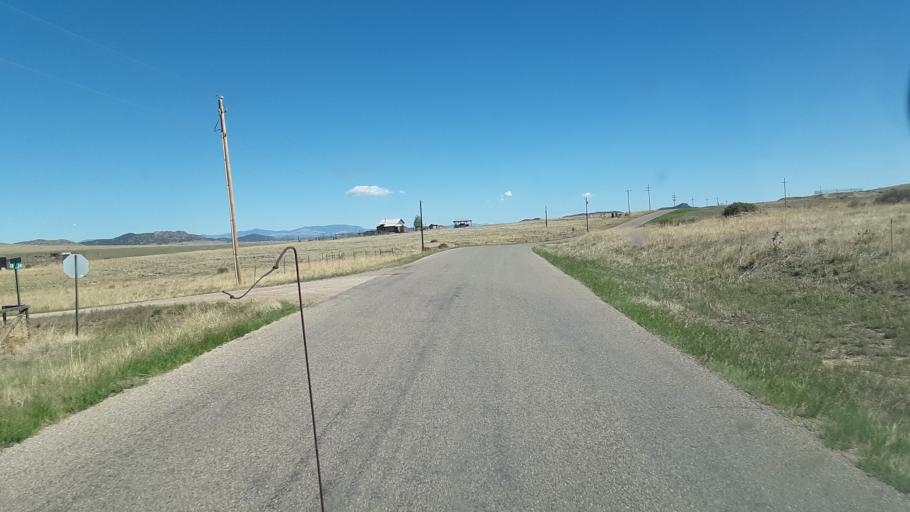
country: US
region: Colorado
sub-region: Custer County
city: Westcliffe
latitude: 38.1579
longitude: -105.4660
